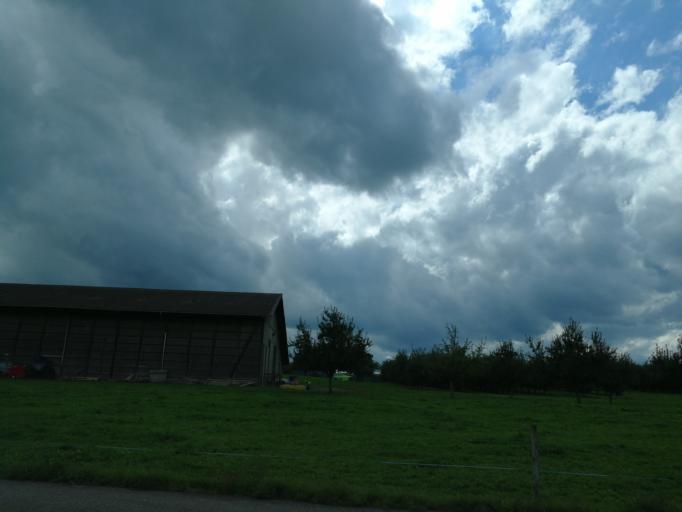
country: CH
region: Thurgau
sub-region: Weinfelden District
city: Sulgen
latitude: 47.5129
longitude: 9.1891
